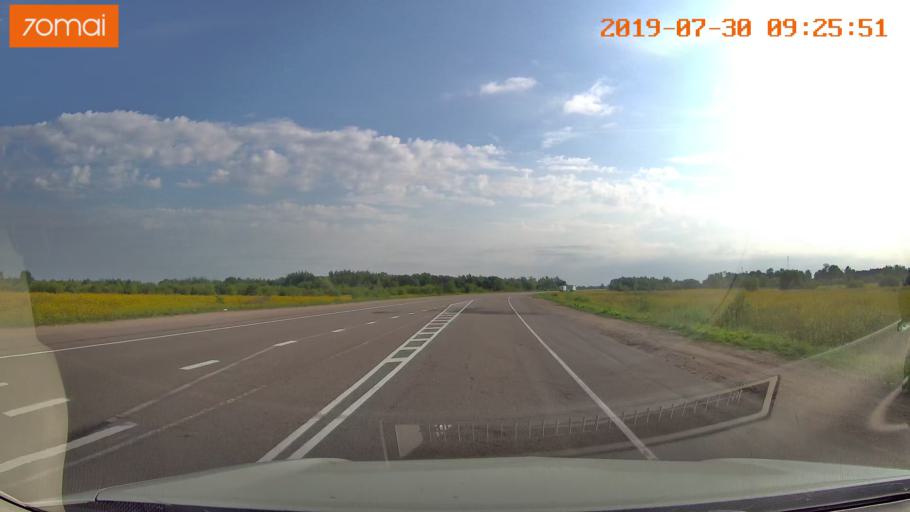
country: LT
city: Kybartai
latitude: 54.6439
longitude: 22.7222
